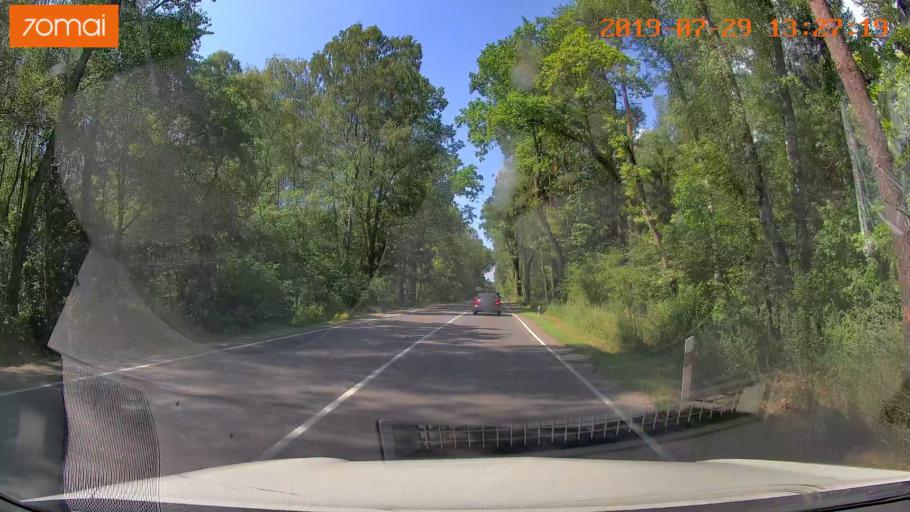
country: RU
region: Kaliningrad
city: Vzmorye
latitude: 54.7047
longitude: 20.3017
